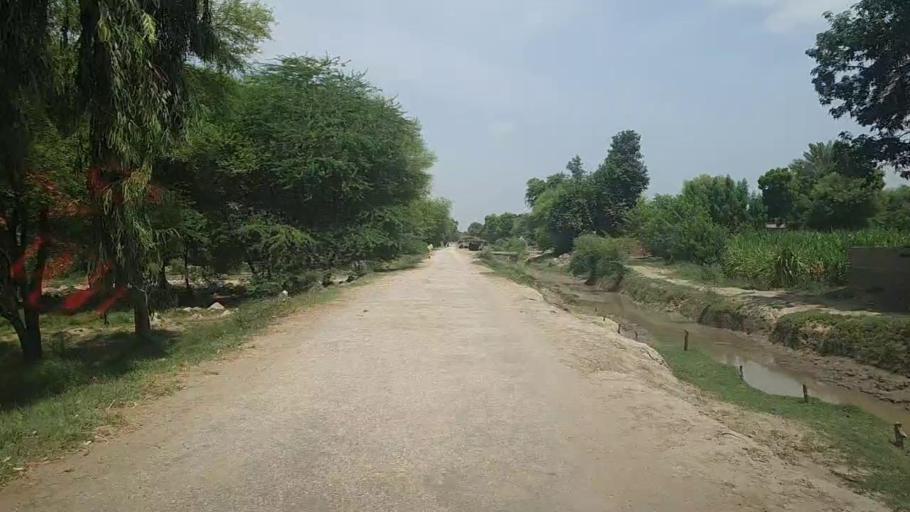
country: PK
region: Sindh
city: Ubauro
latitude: 28.2919
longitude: 69.8003
